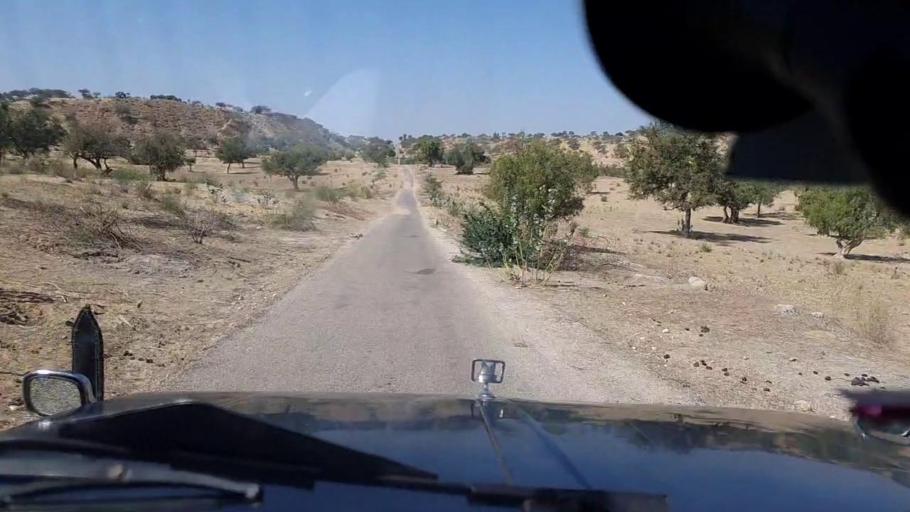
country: PK
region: Sindh
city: Mithi
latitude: 24.6123
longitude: 69.7173
